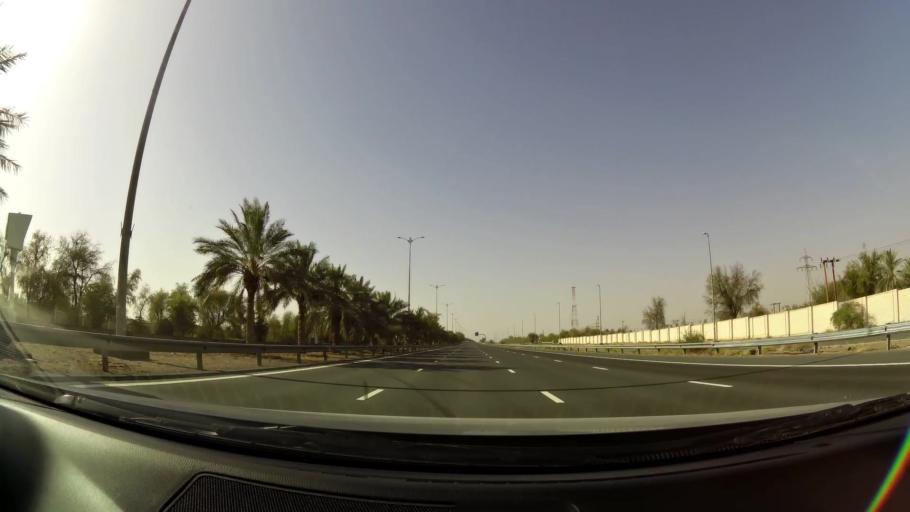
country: OM
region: Al Buraimi
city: Al Buraymi
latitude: 24.4210
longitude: 55.7908
